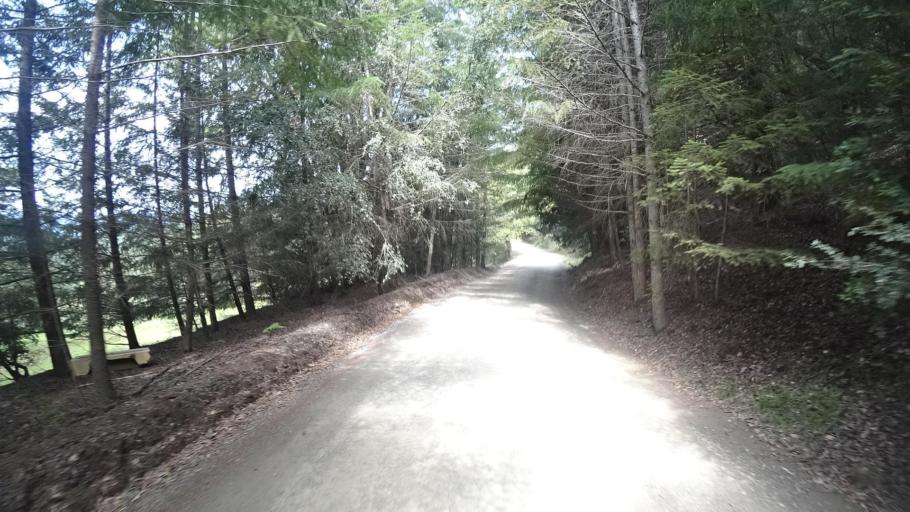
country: US
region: California
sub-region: Humboldt County
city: Redway
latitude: 40.0383
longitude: -123.8418
